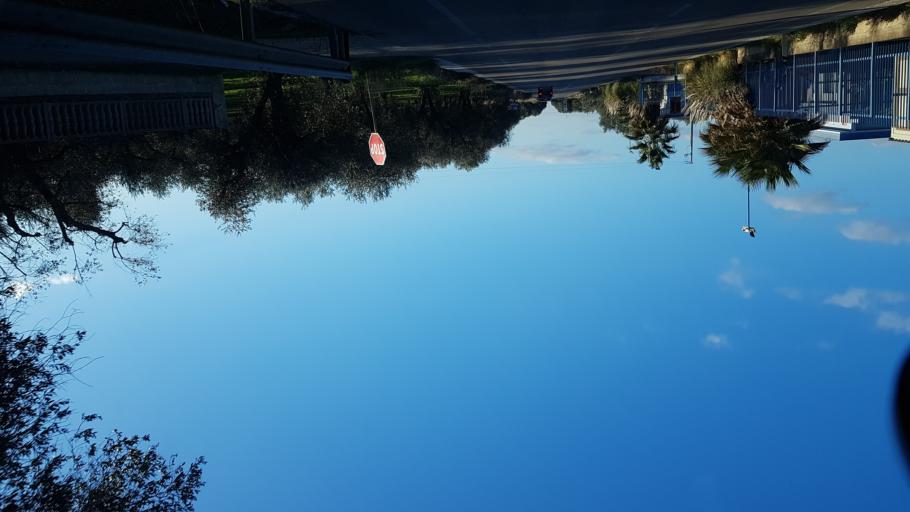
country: IT
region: Apulia
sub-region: Provincia di Brindisi
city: San Pietro Vernotico
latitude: 40.4743
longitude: 18.0099
